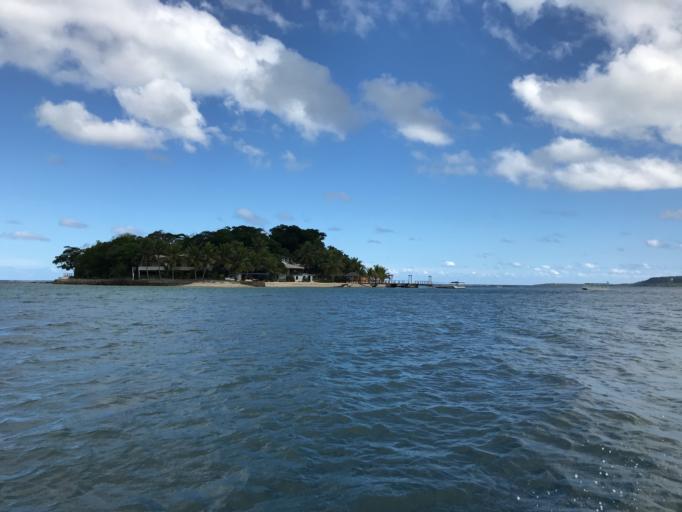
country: VU
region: Shefa
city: Port-Vila
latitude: -17.6949
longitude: 168.2644
